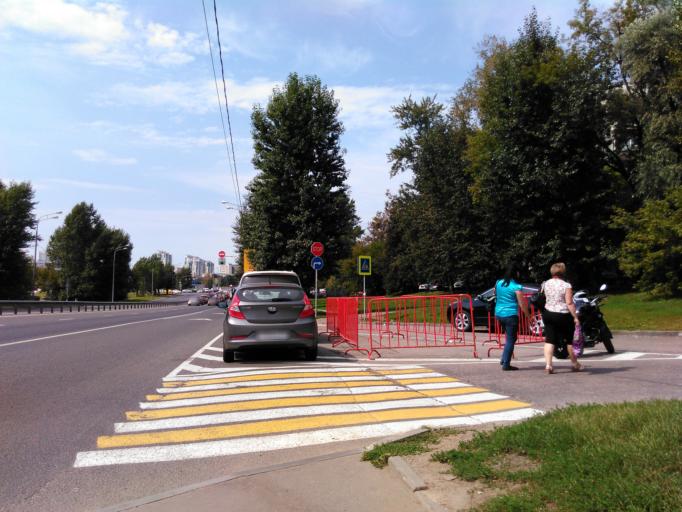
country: RU
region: Moscow
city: Troparevo
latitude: 55.6695
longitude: 37.4990
